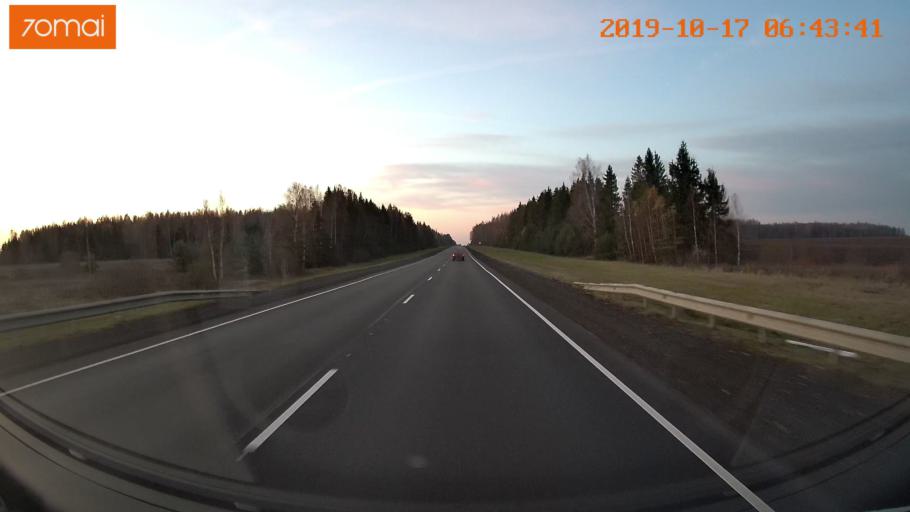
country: RU
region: Vladimir
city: Kideksha
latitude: 56.5838
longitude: 40.5550
